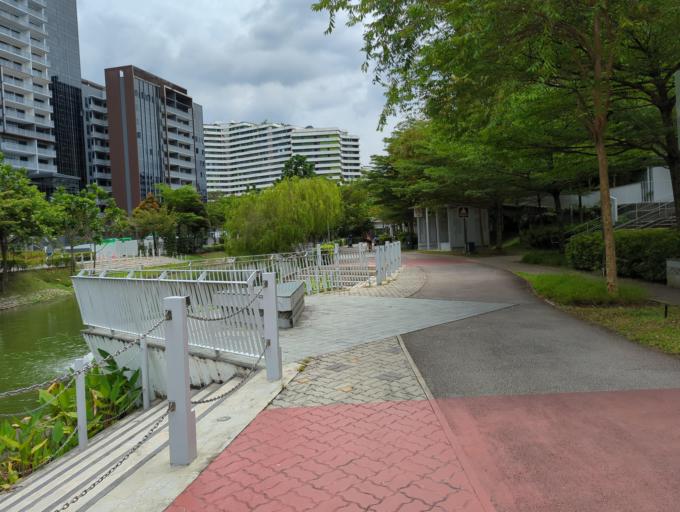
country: MY
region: Johor
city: Kampung Pasir Gudang Baru
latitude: 1.4094
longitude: 103.8974
